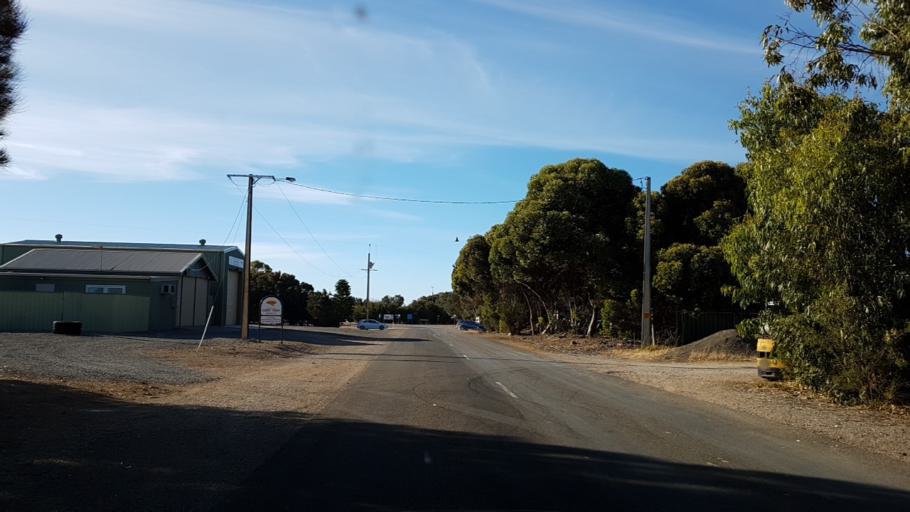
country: AU
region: South Australia
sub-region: Yorke Peninsula
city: Port Victoria
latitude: -34.9267
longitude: 137.0843
